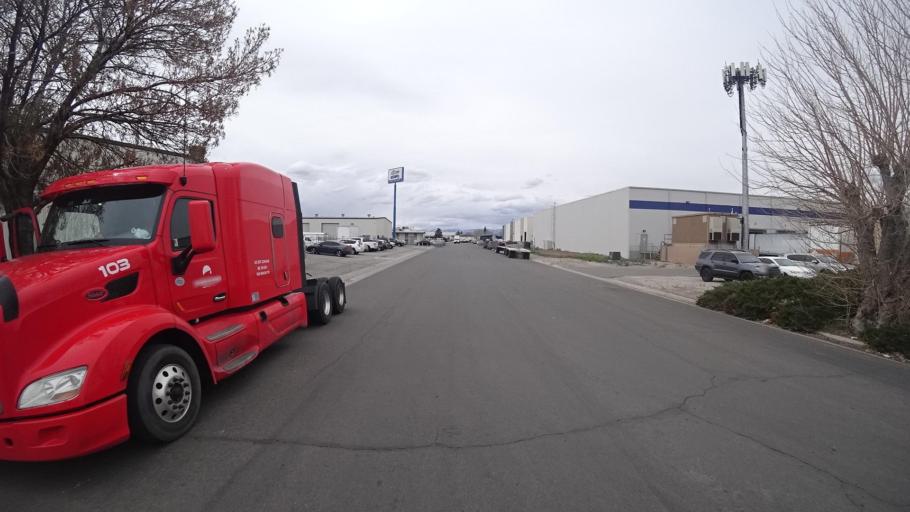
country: US
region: Nevada
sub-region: Washoe County
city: Sparks
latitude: 39.5253
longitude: -119.7362
